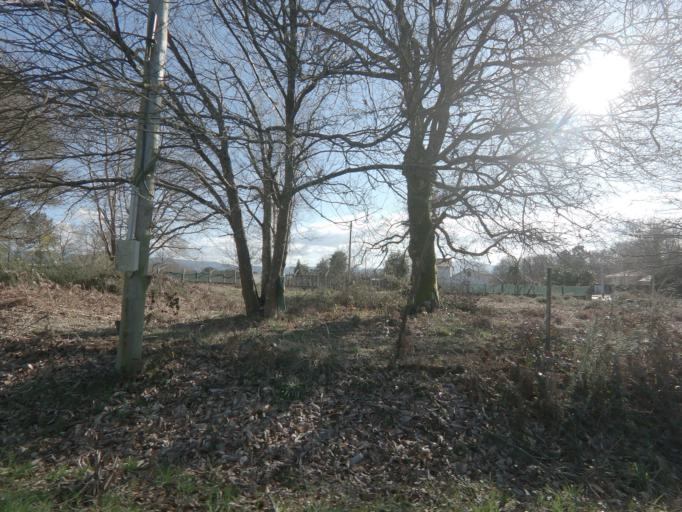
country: ES
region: Galicia
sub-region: Provincia da Coruna
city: Ribeira
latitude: 42.7135
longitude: -8.4454
